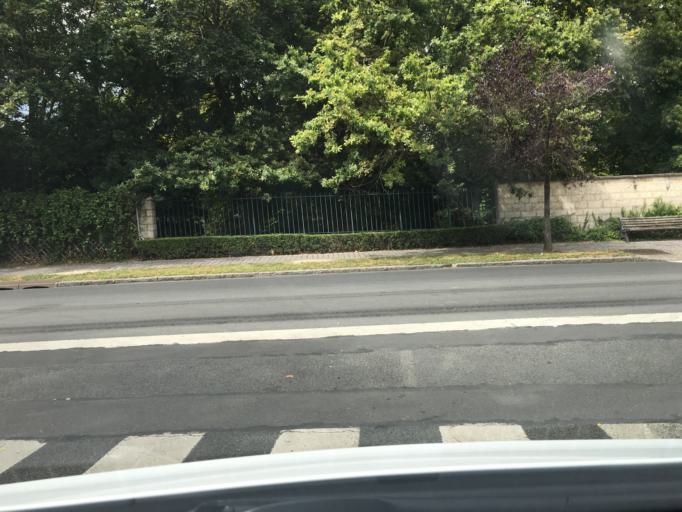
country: FR
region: Ile-de-France
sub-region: Departement des Hauts-de-Seine
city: Rueil-Malmaison
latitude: 48.8719
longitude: 2.1768
